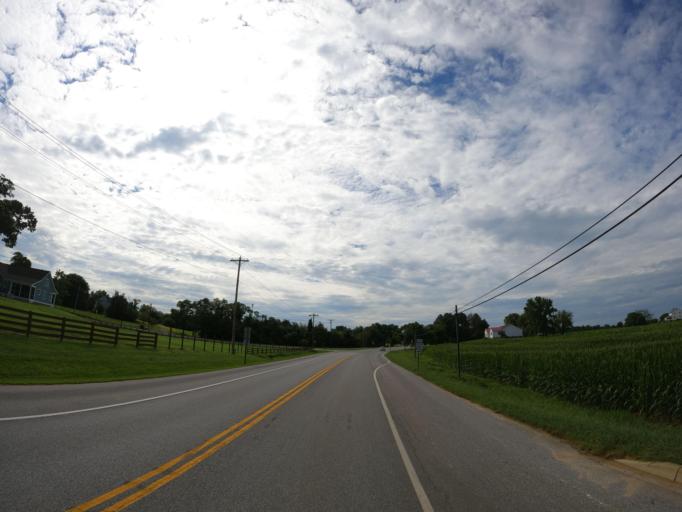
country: US
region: Maryland
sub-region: Saint Mary's County
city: Leonardtown
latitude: 38.3650
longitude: -76.6834
